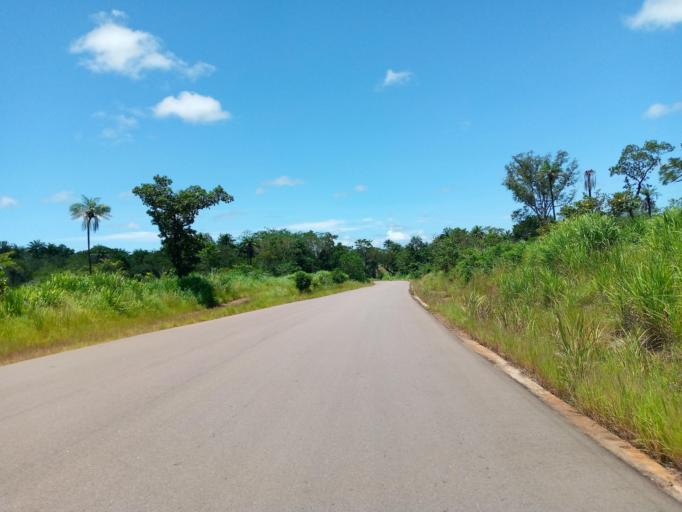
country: SL
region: Northern Province
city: Makeni
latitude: 9.0959
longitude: -12.1979
